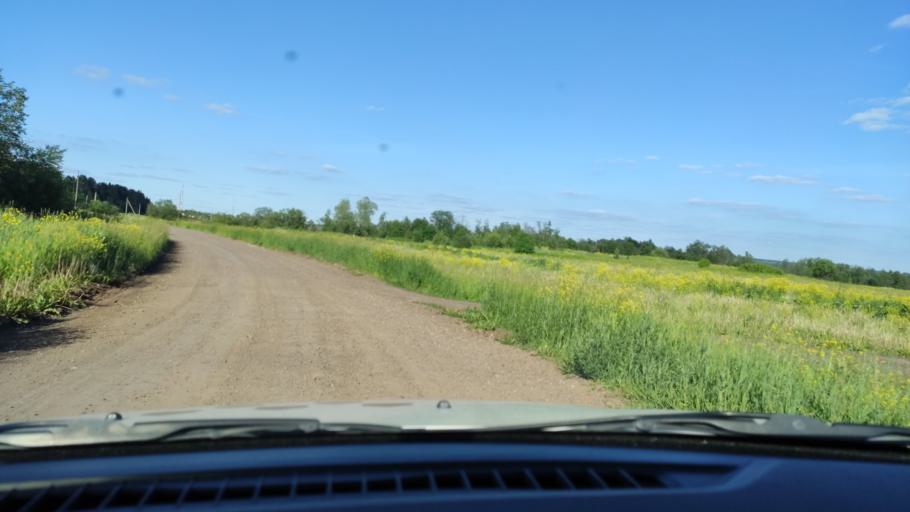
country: RU
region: Perm
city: Orda
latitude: 57.3003
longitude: 56.6254
